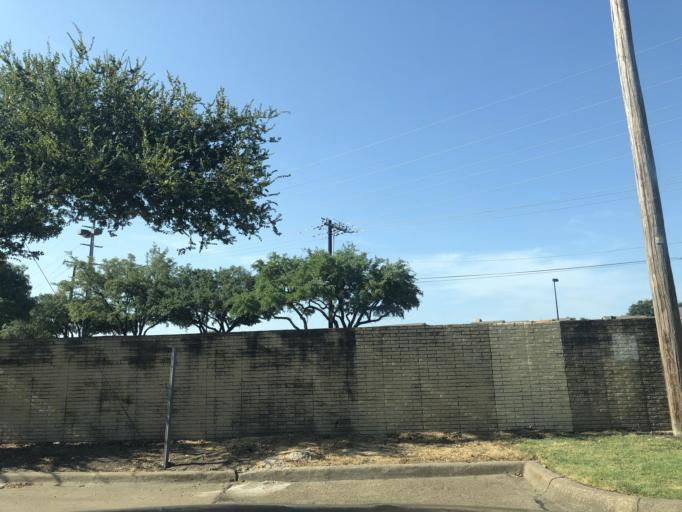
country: US
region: Texas
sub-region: Dallas County
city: Garland
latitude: 32.8644
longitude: -96.6456
